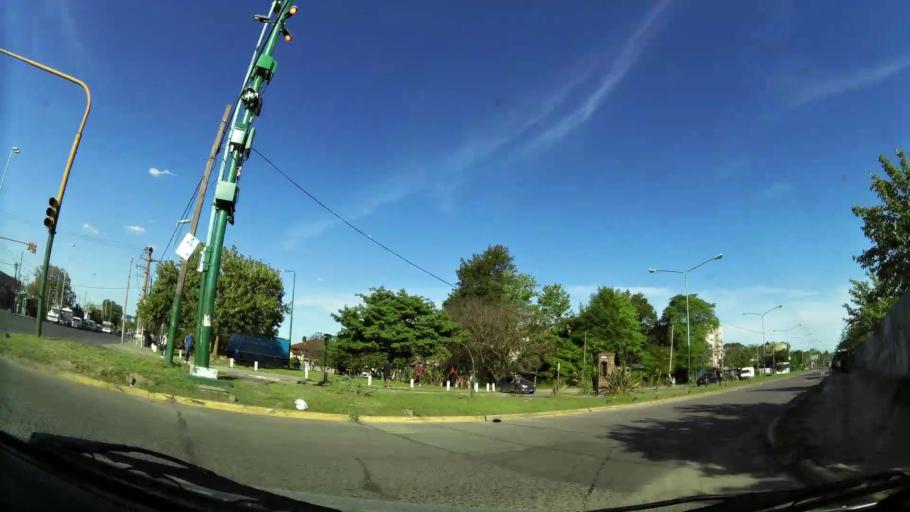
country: AR
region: Buenos Aires
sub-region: Partido de Almirante Brown
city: Adrogue
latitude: -34.8063
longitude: -58.3385
